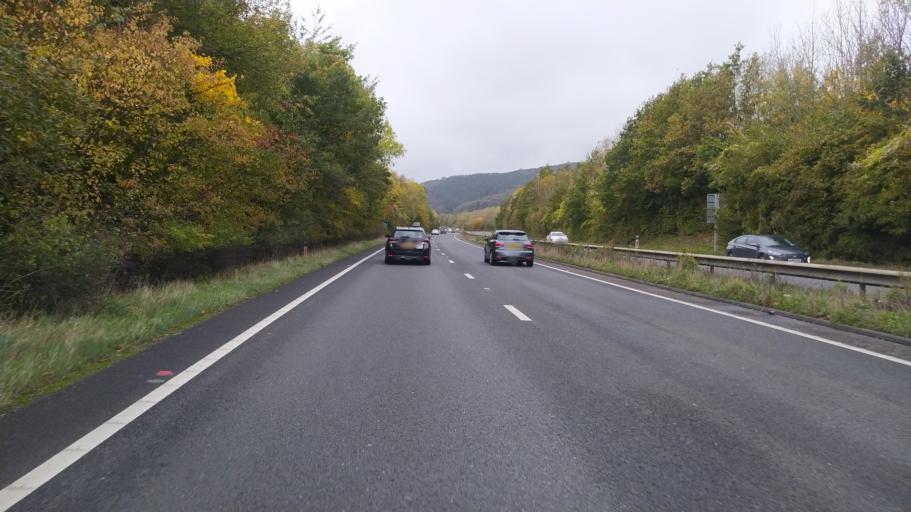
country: GB
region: England
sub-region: Hampshire
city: Petersfield
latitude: 50.9871
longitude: -0.9593
